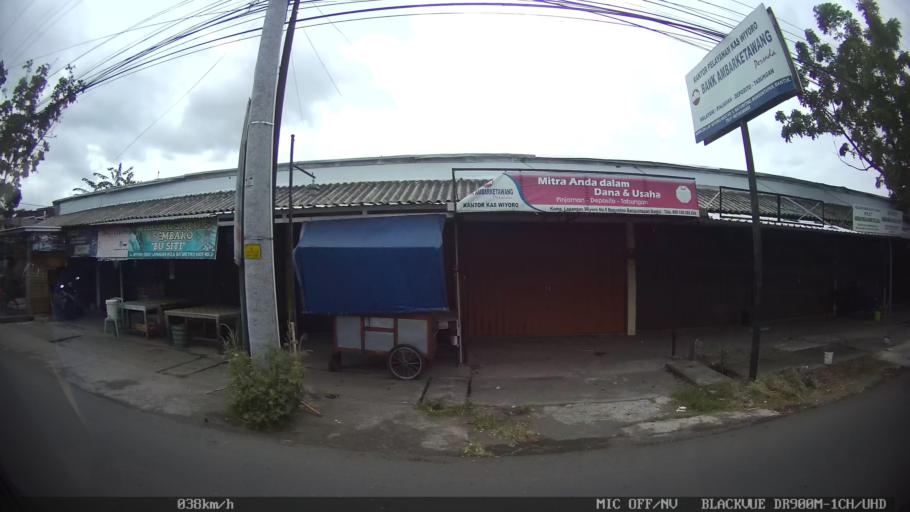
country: ID
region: Daerah Istimewa Yogyakarta
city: Depok
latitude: -7.8229
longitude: 110.4147
